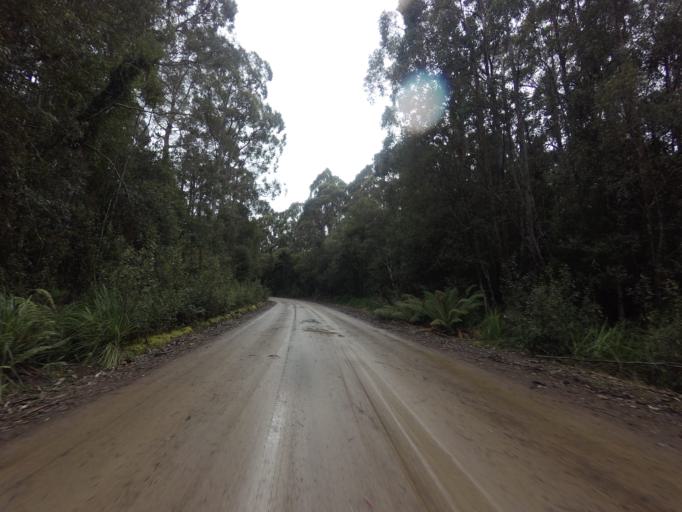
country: AU
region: Tasmania
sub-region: Huon Valley
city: Geeveston
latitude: -43.4929
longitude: 146.8873
